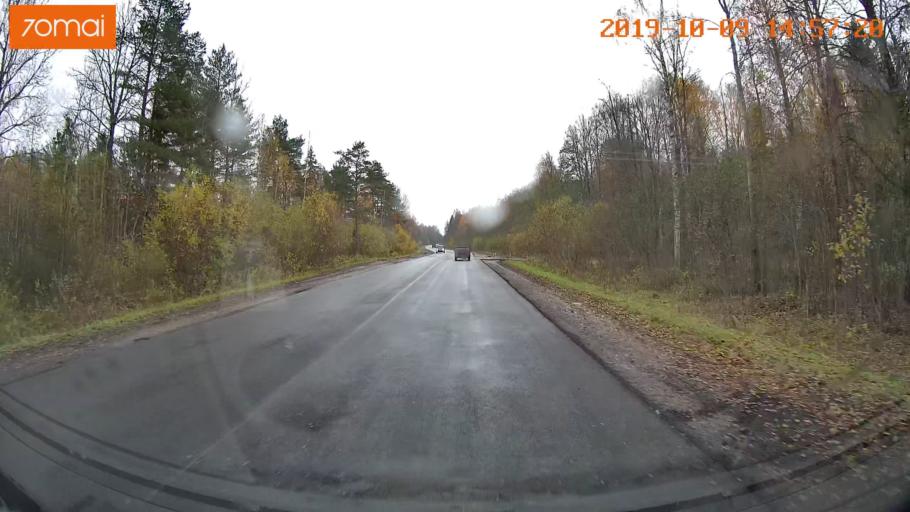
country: RU
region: Kostroma
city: Chistyye Bory
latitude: 58.3387
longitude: 41.6502
